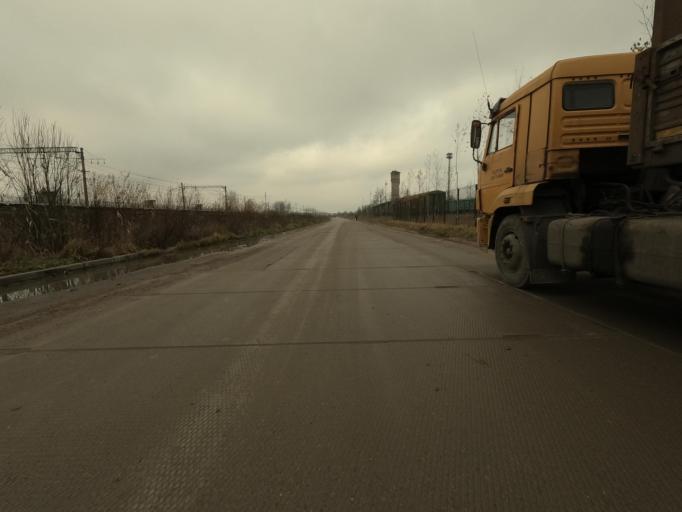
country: RU
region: Leningrad
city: Lyuban'
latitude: 59.4689
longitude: 31.2535
